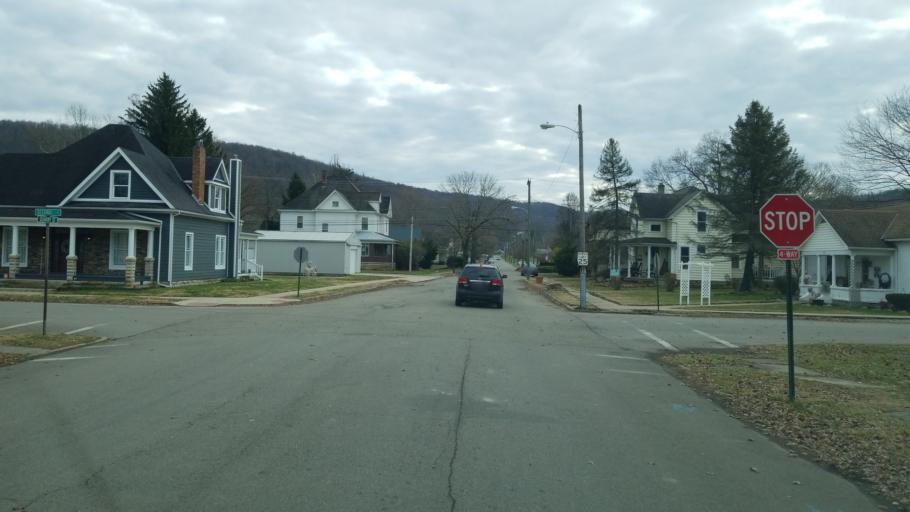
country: US
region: Ohio
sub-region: Highland County
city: Greenfield
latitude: 39.2272
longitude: -83.2701
